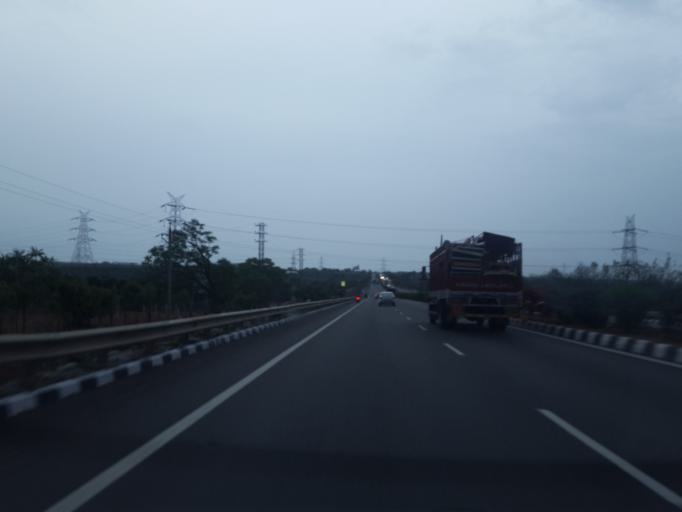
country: IN
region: Telangana
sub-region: Mahbubnagar
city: Farrukhnagar
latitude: 17.0969
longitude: 78.2470
